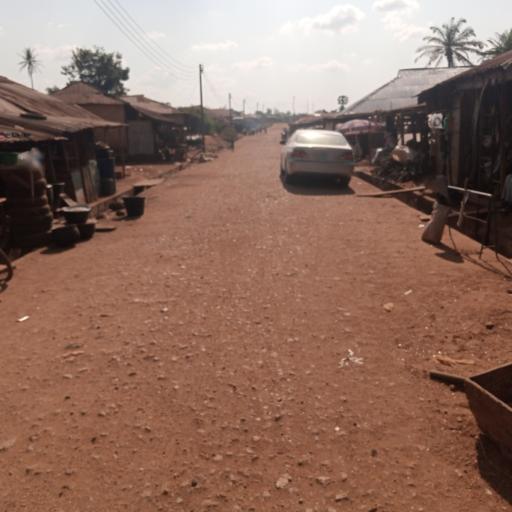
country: NG
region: Osun
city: Modakeke
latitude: 7.1726
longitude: 4.3605
